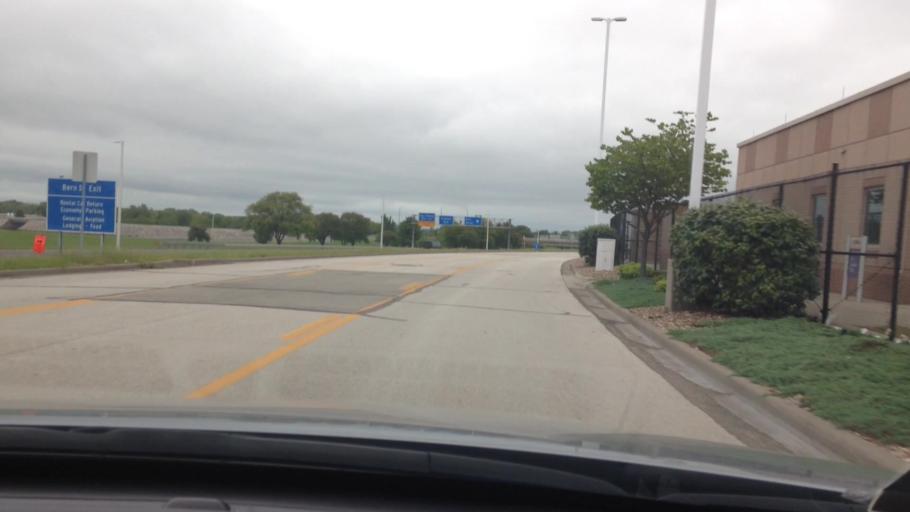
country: US
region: Missouri
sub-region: Platte County
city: Weatherby Lake
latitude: 39.3059
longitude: -94.7101
